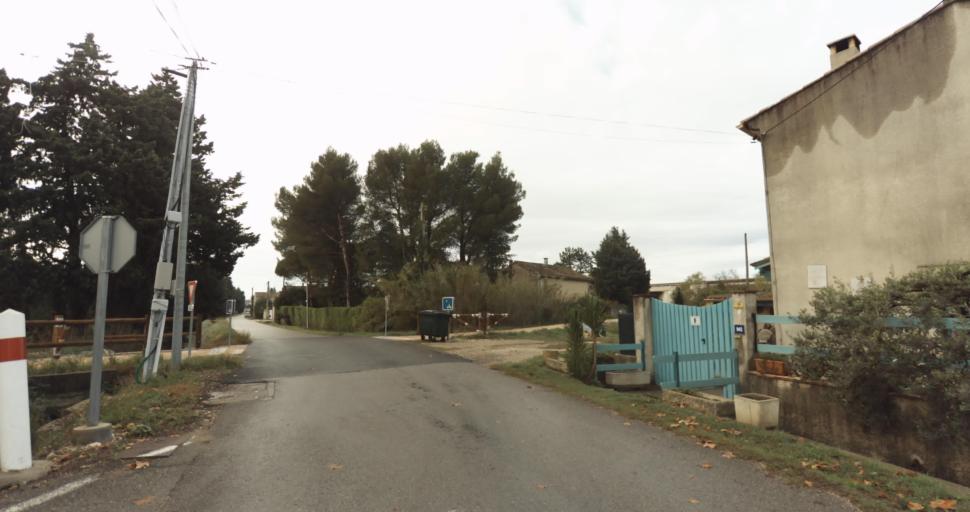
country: FR
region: Provence-Alpes-Cote d'Azur
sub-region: Departement des Bouches-du-Rhone
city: Rognonas
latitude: 43.9007
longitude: 4.7875
